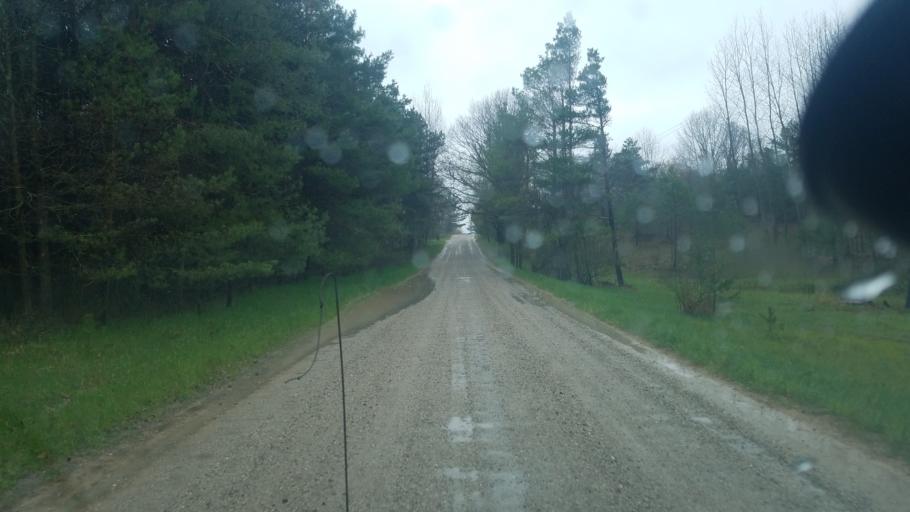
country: US
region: Michigan
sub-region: Montcalm County
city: Lakeview
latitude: 43.4689
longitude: -85.2937
